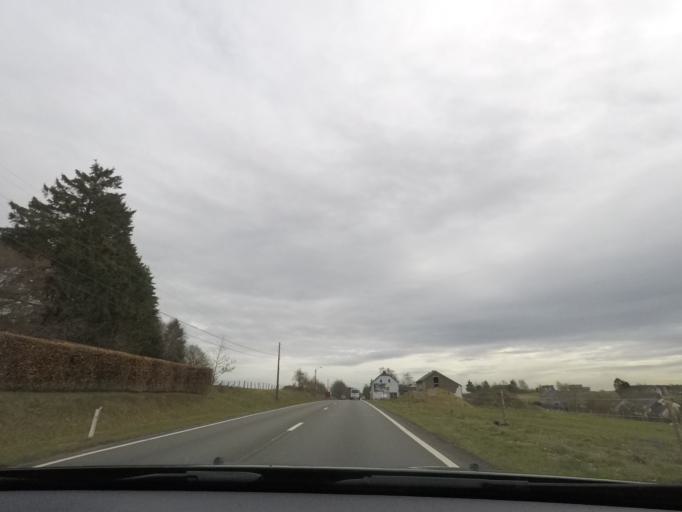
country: LU
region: Diekirch
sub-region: Canton de Wiltz
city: Bavigne
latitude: 49.9856
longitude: 5.8221
